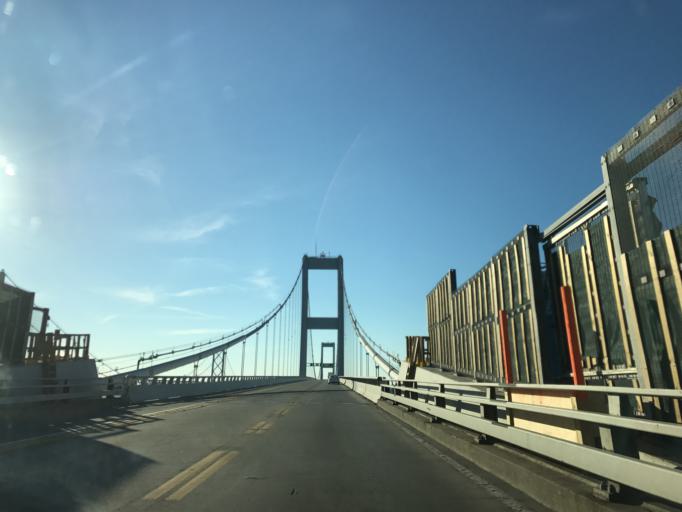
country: US
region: Maryland
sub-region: Queen Anne's County
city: Stevensville
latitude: 38.9932
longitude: -76.3764
